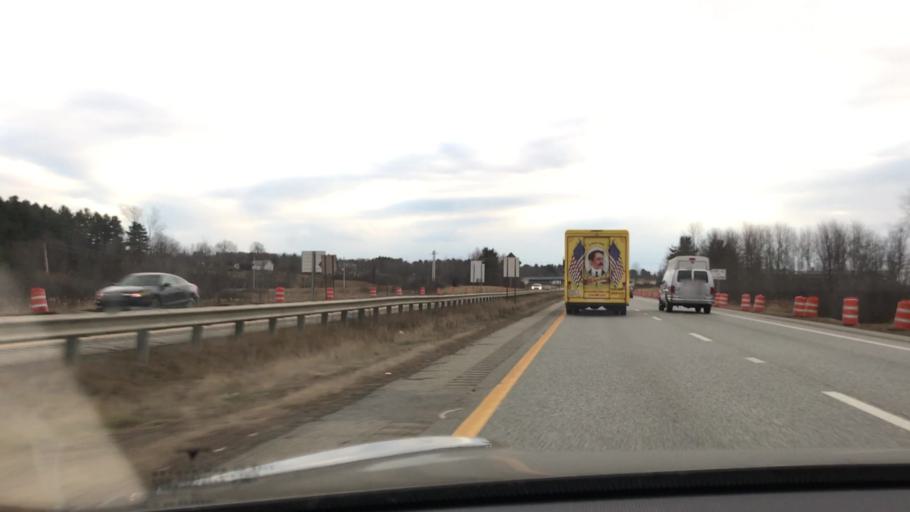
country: US
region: Maine
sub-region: Kennebec County
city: Hallowell
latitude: 44.3018
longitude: -69.8077
